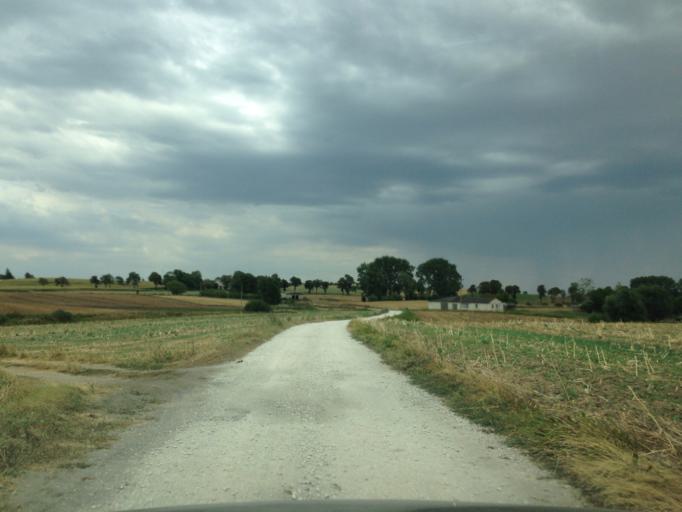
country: PL
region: Kujawsko-Pomorskie
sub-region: Powiat golubsko-dobrzynski
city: Kowalewo Pomorskie
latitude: 53.1769
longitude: 18.8368
